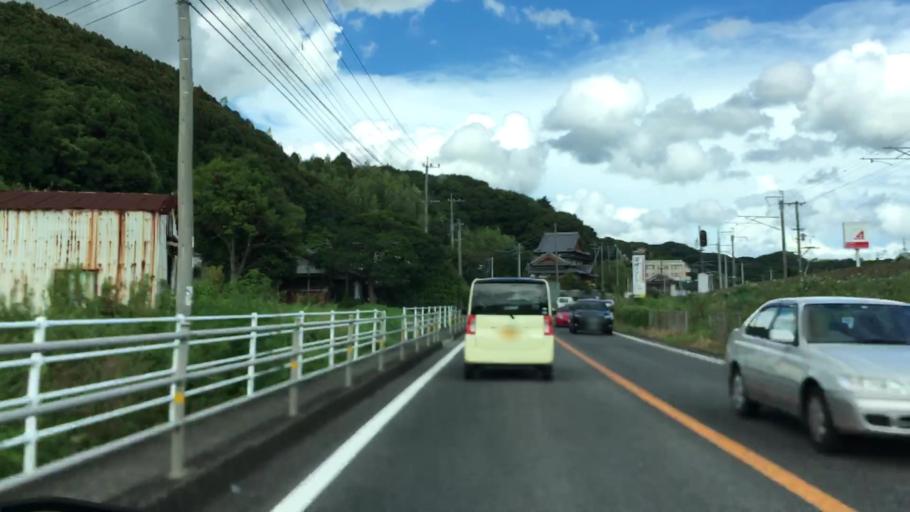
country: JP
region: Nagasaki
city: Sasebo
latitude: 33.1449
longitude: 129.8181
